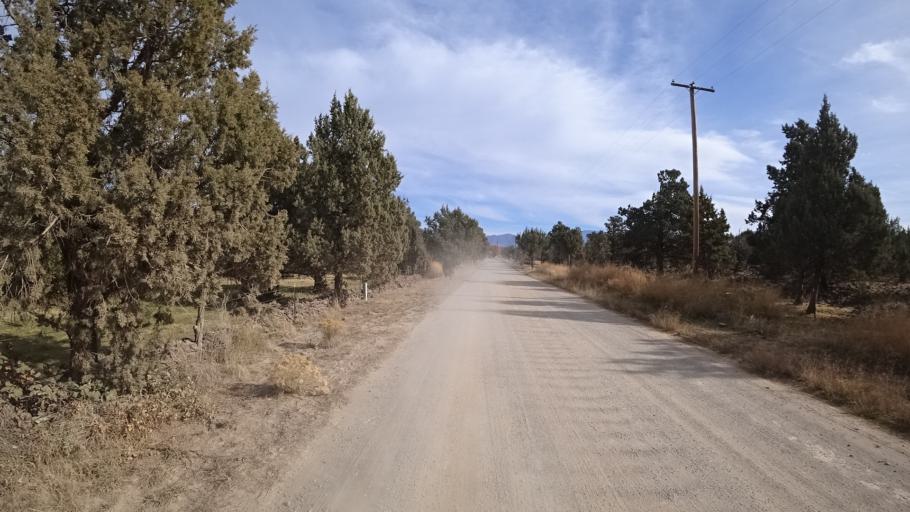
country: US
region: California
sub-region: Siskiyou County
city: Weed
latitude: 41.5955
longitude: -122.4136
